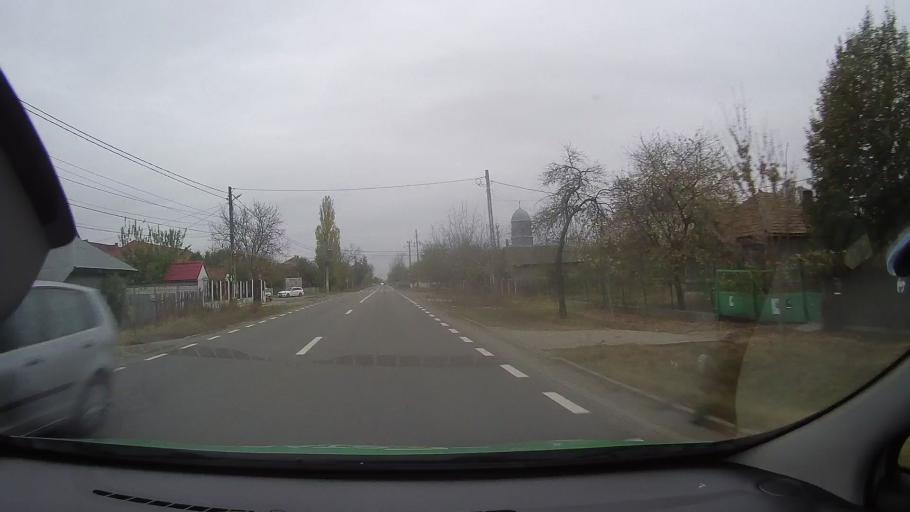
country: RO
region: Ialomita
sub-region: Comuna Slobozia
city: Slobozia
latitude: 44.6032
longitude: 27.3872
